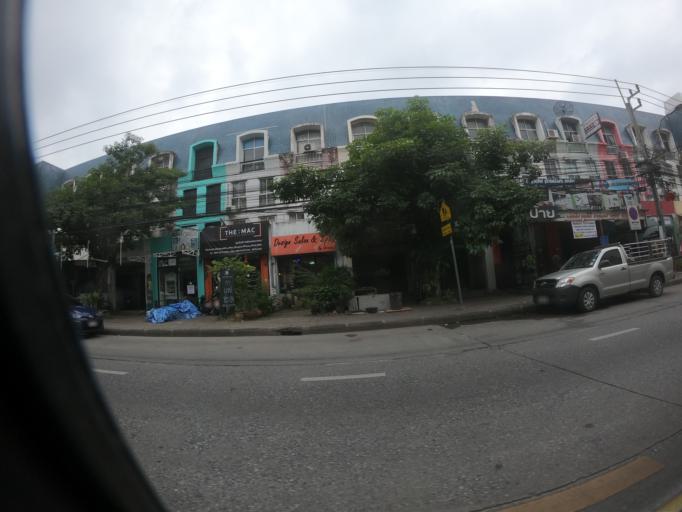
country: TH
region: Bangkok
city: Lat Phrao
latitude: 13.8240
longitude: 100.6158
